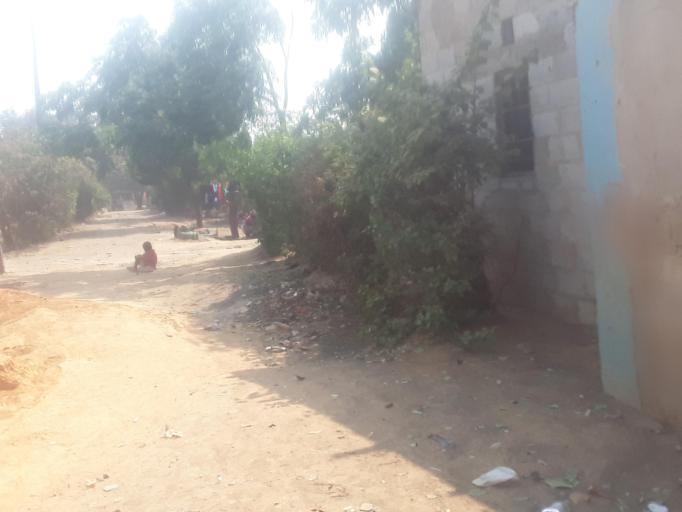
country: ZM
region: Lusaka
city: Lusaka
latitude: -15.3532
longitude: 28.2897
